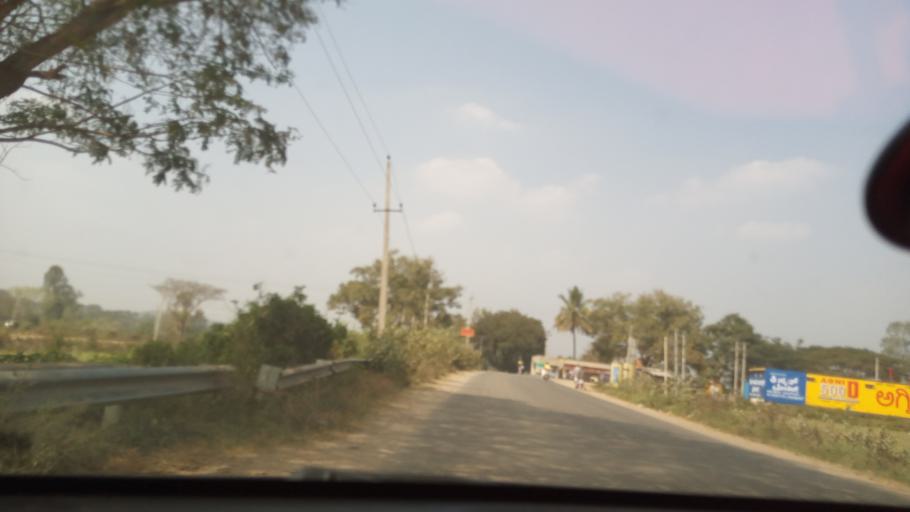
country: IN
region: Karnataka
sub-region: Mysore
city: Nanjangud
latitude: 12.1170
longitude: 76.7021
